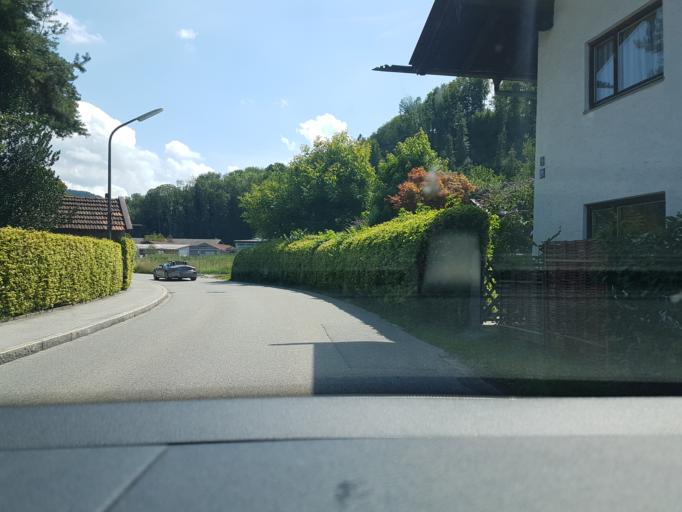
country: DE
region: Bavaria
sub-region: Upper Bavaria
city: Altenmarkt
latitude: 47.7804
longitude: 12.1378
